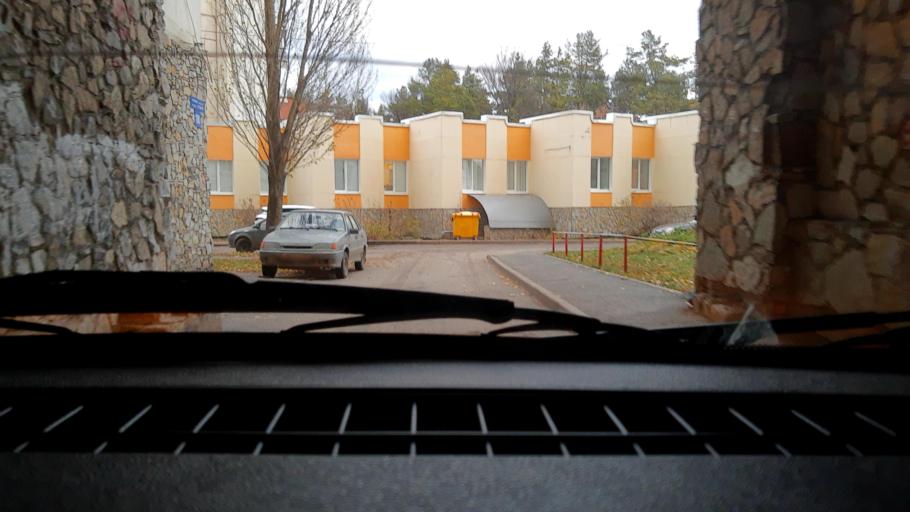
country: RU
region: Bashkortostan
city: Ufa
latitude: 54.7941
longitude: 56.0416
